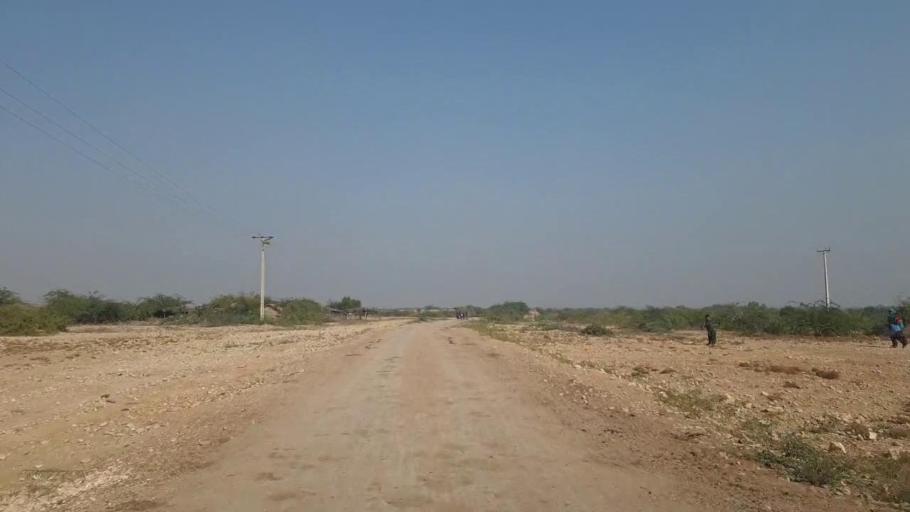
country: PK
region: Sindh
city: Matiari
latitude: 25.5438
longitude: 68.3518
